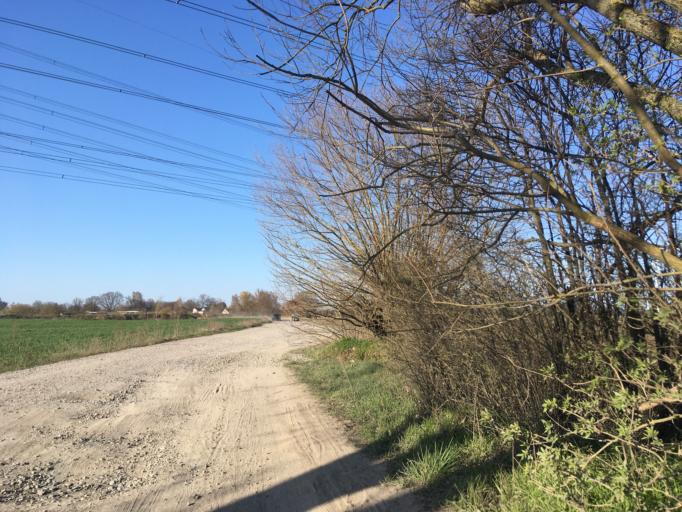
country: DE
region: Brandenburg
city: Ahrensfelde
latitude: 52.6202
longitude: 13.5737
